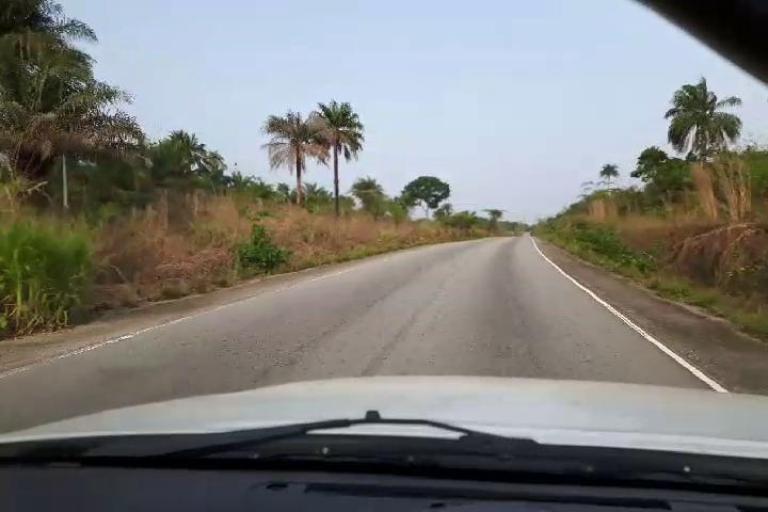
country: SL
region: Eastern Province
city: Blama
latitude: 7.9399
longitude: -11.4988
